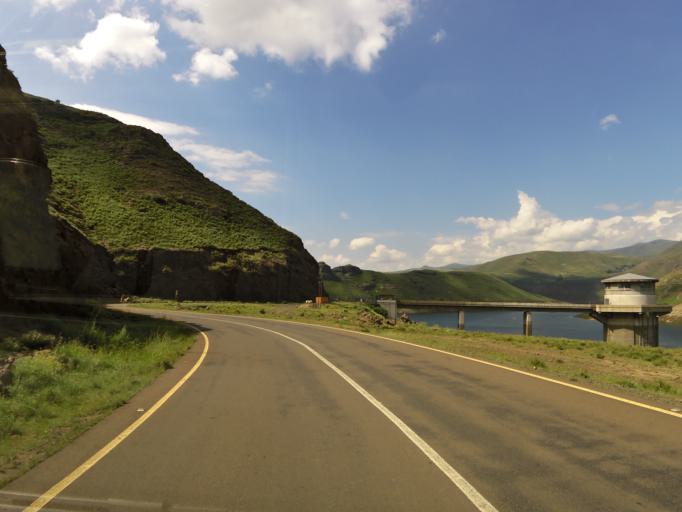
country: LS
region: Thaba-Tseka
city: Thaba-Tseka
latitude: -29.1737
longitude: 28.4808
